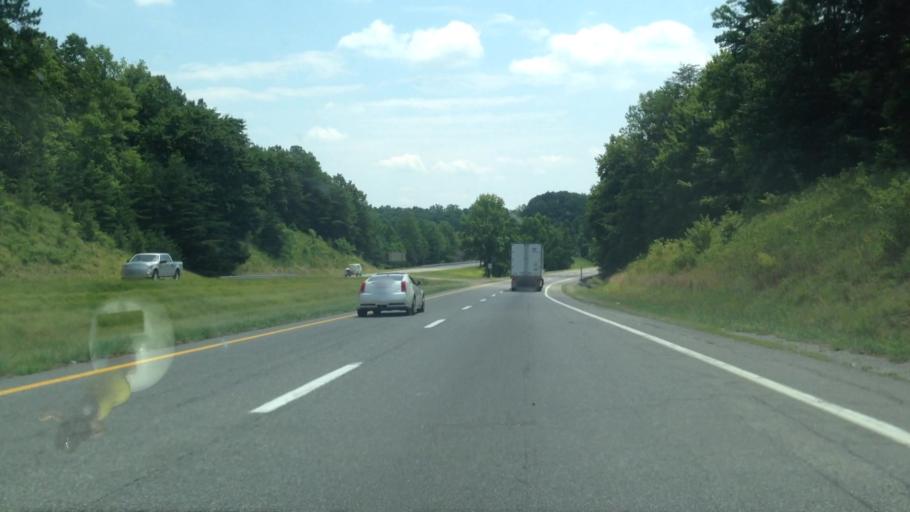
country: US
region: Virginia
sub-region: Henry County
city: Horse Pasture
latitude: 36.6469
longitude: -79.9085
